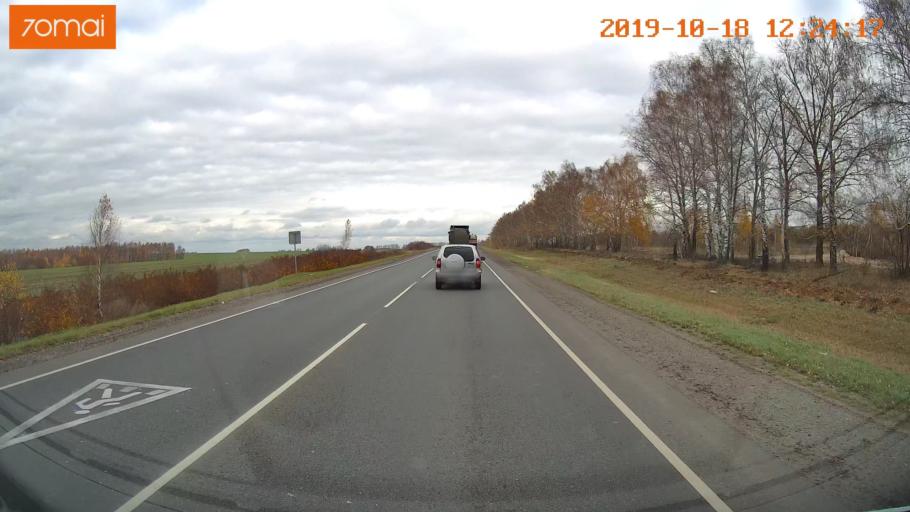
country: RU
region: Rjazan
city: Rybnoye
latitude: 54.5378
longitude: 39.5127
